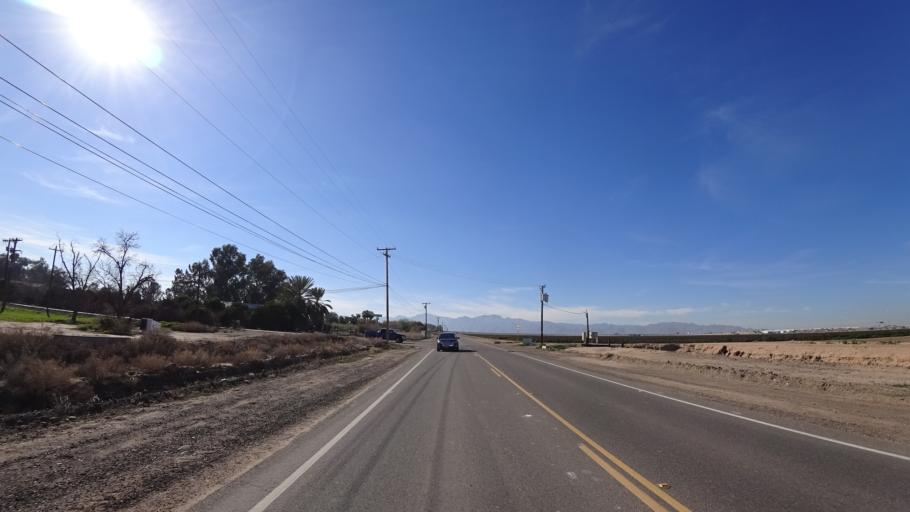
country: US
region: Arizona
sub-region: Maricopa County
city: Citrus Park
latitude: 33.5516
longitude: -112.4019
